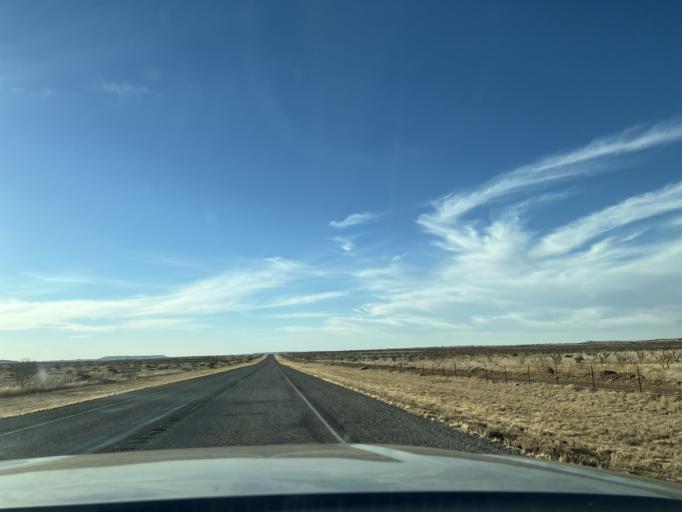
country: US
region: Texas
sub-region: Borden County
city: Gail
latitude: 32.7624
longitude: -101.2714
